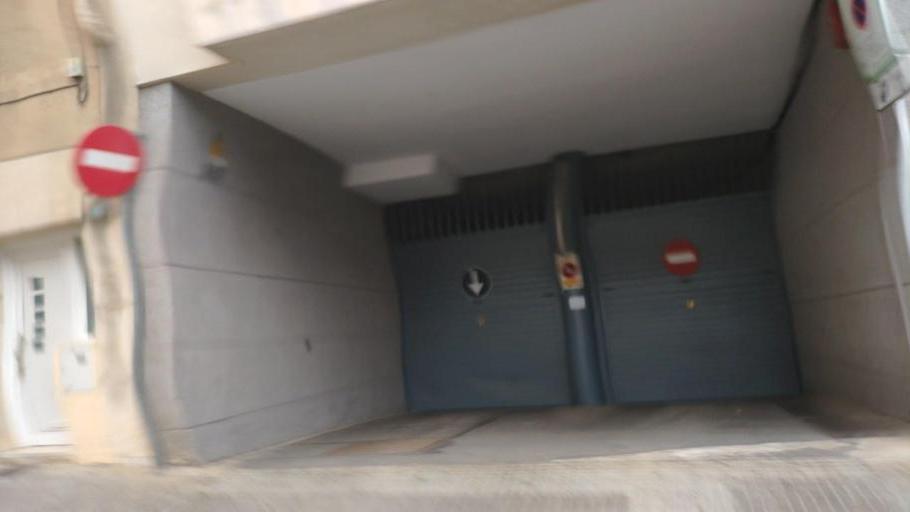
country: ES
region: Catalonia
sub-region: Provincia de Barcelona
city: Sant Cugat del Valles
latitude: 41.4764
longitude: 2.0902
